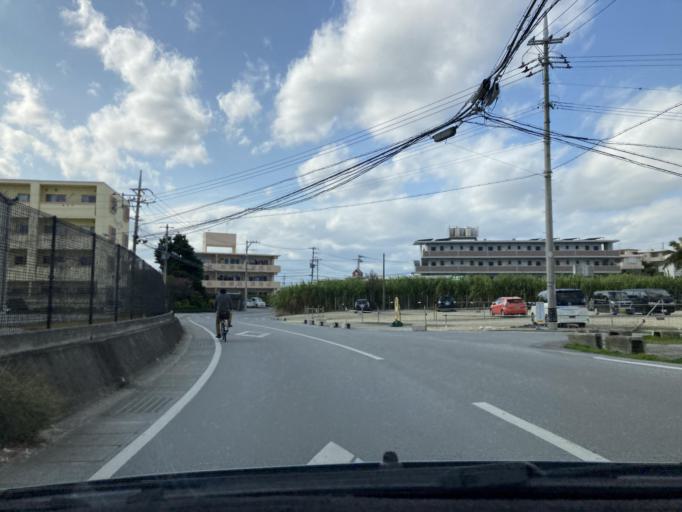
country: JP
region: Okinawa
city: Tomigusuku
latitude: 26.1955
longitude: 127.7479
